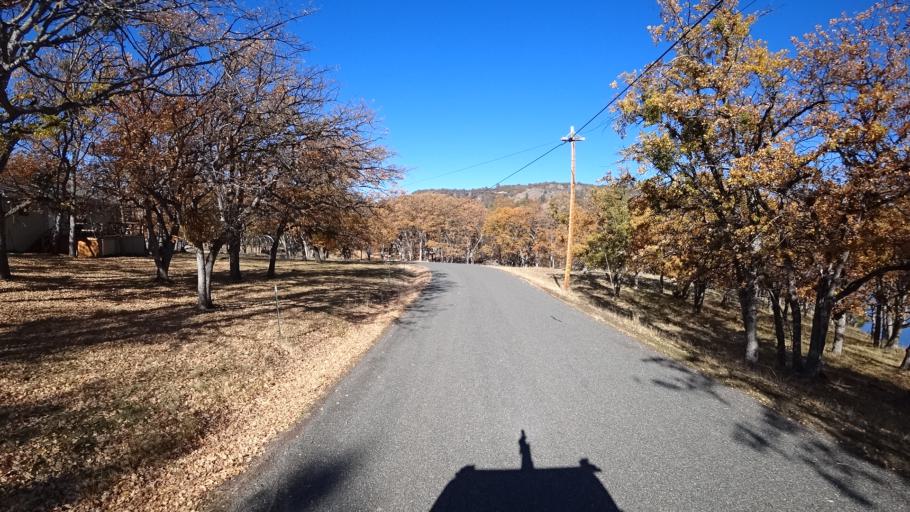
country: US
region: California
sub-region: Siskiyou County
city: Montague
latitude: 41.9784
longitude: -122.3244
